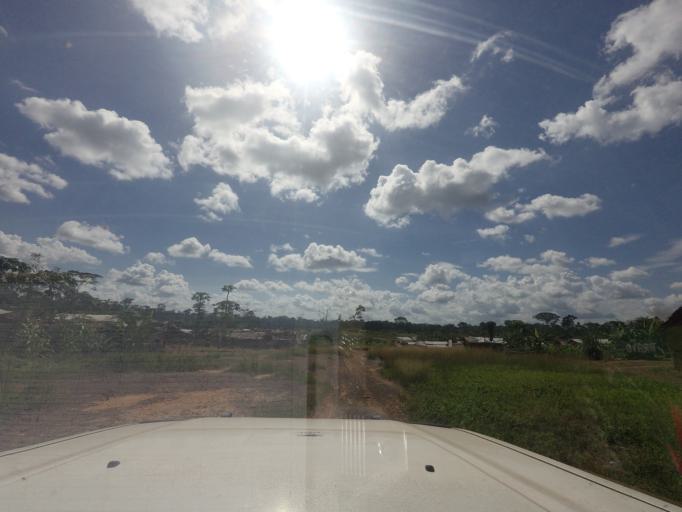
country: LR
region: Grand Gedeh
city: Zwedru
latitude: 6.0374
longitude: -8.0514
